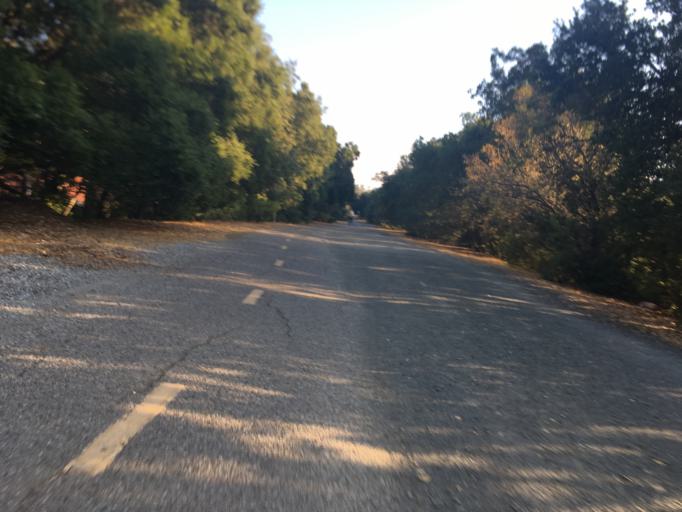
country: US
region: California
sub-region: Santa Clara County
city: Los Altos Hills
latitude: 37.4012
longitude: -122.1353
